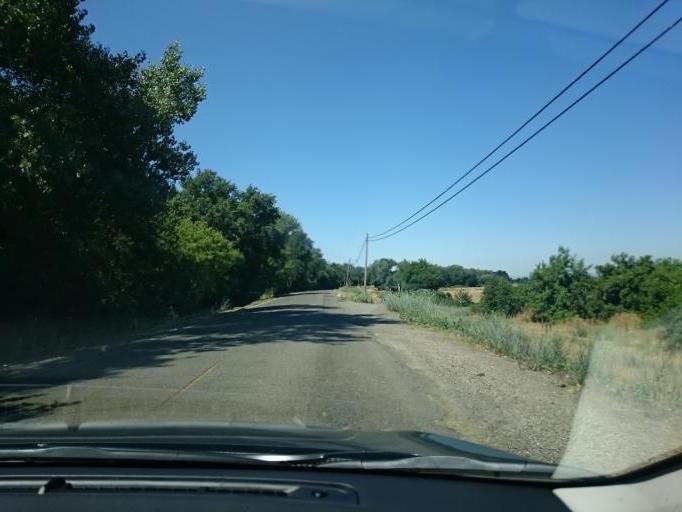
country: US
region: California
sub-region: Yolo County
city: West Sacramento
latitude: 38.5390
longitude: -121.5164
